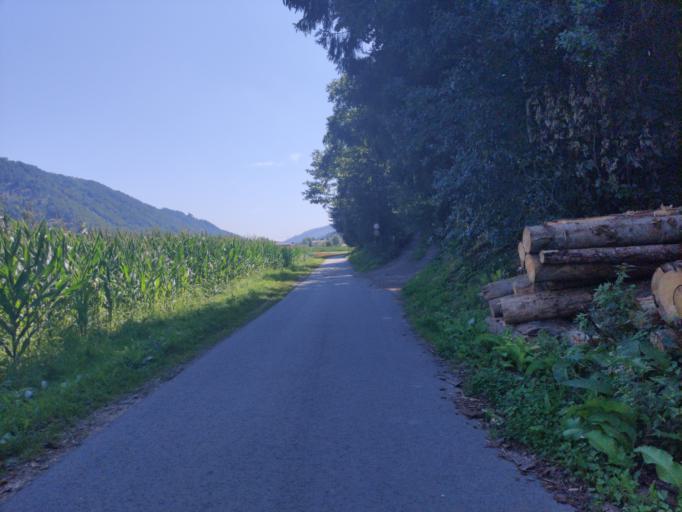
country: AT
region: Upper Austria
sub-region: Politischer Bezirk Rohrbach
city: Pfarrkirchen im Muehlkreis
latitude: 48.4937
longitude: 13.7388
